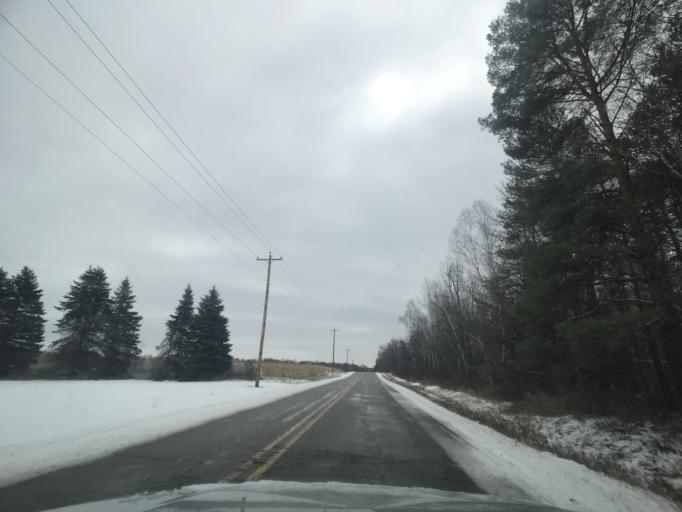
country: US
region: Wisconsin
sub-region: Brown County
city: Suamico
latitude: 44.7175
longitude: -88.0709
